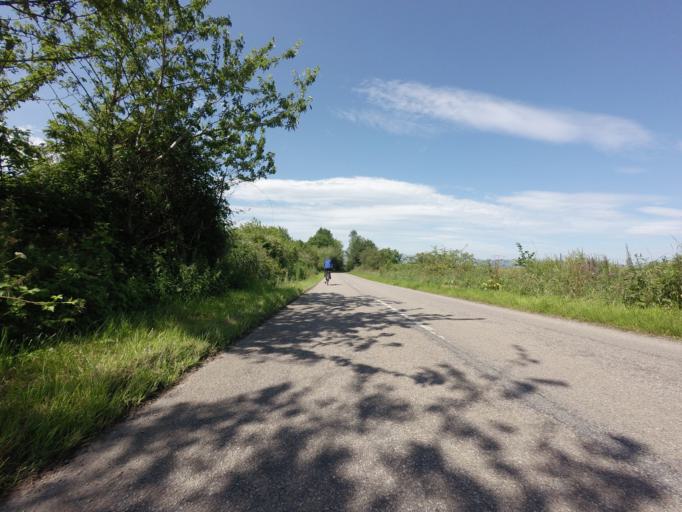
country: GB
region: Scotland
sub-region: Highland
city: Conon Bridge
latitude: 57.5534
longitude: -4.4060
